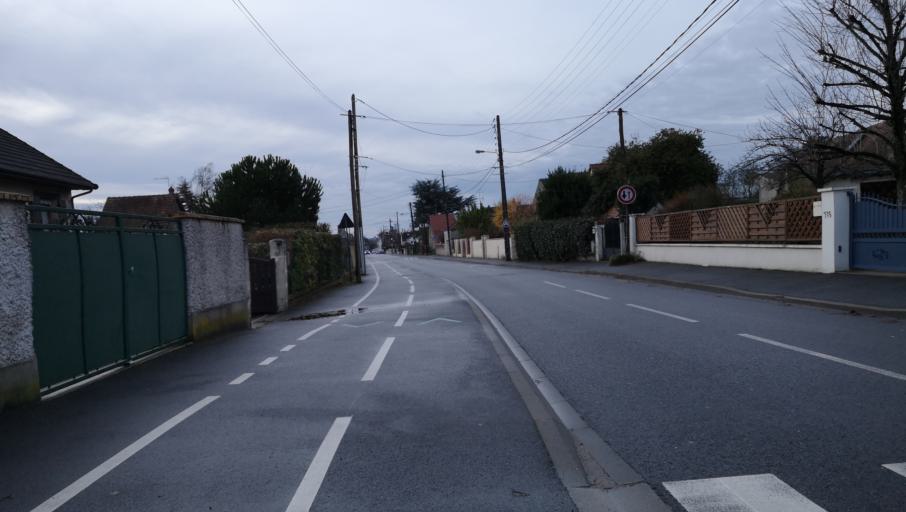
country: FR
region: Centre
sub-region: Departement du Loiret
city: Saint-Jean-de-Braye
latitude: 47.9206
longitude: 1.9651
